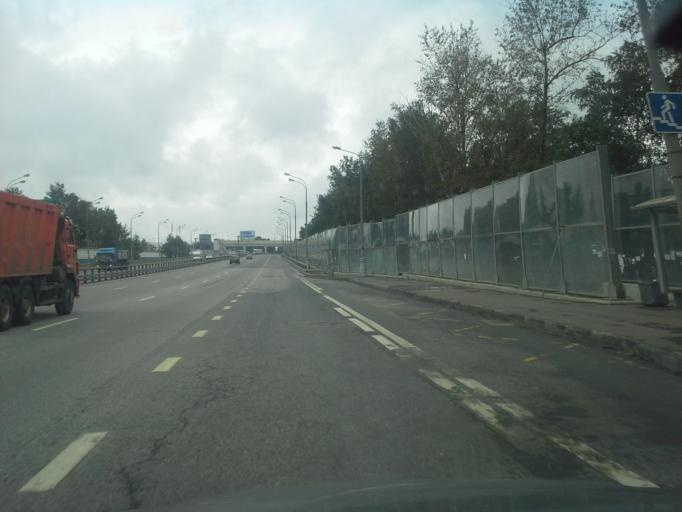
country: RU
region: Moskovskaya
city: Annino
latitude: 55.6010
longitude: 37.2447
